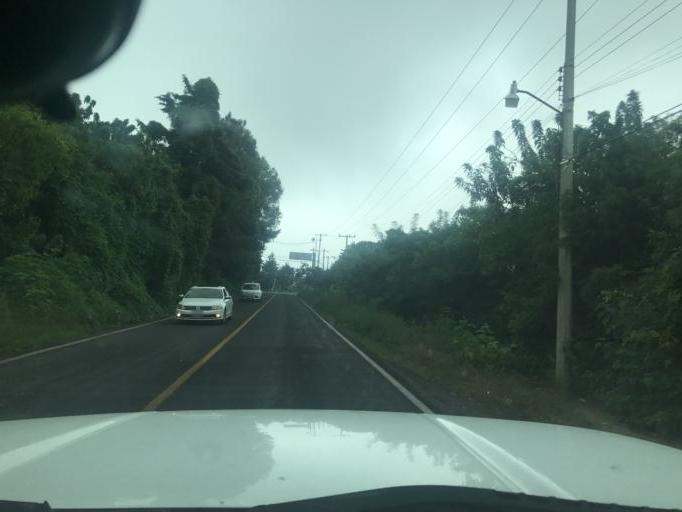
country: MX
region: Morelos
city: Ocuituco
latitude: 18.8818
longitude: -98.7641
